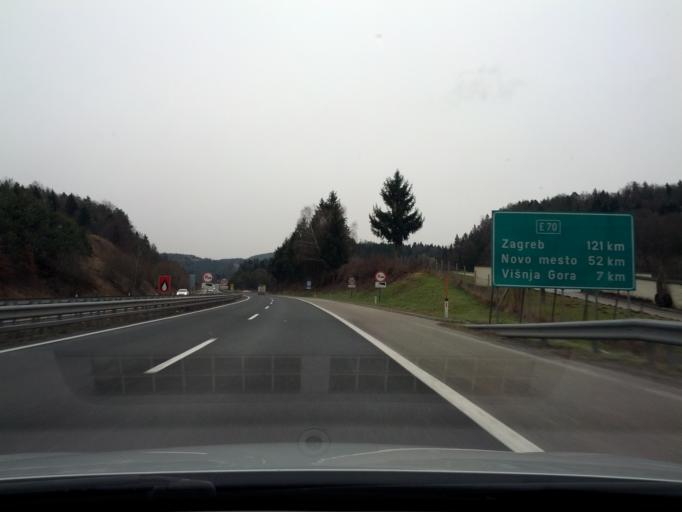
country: SI
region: Grosuplje
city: Grosuplje
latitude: 45.9698
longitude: 14.6644
